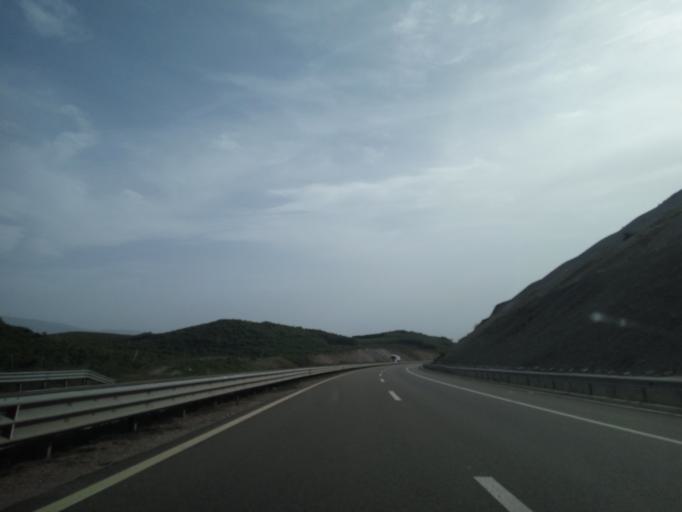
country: XK
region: Prizren
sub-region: Komuna e Therandes
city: Peqan
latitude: 42.3941
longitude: 20.8595
